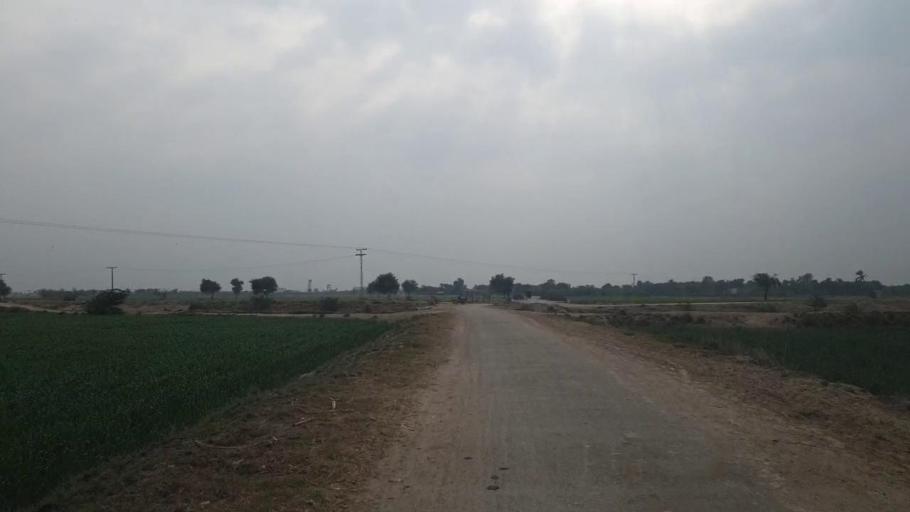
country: PK
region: Sindh
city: Shahdadpur
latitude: 25.9436
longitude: 68.7028
